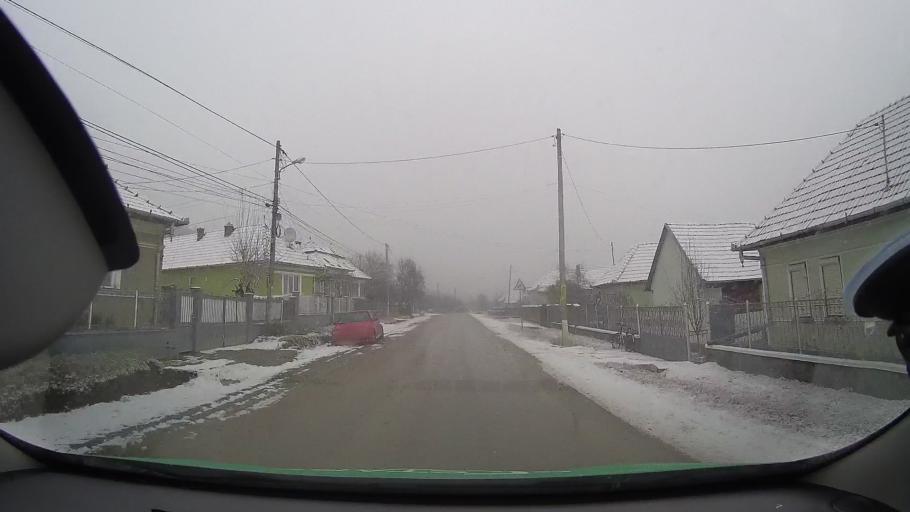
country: RO
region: Alba
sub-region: Comuna Lopadea Noua
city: Lopadea Noua
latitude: 46.2900
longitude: 23.8274
